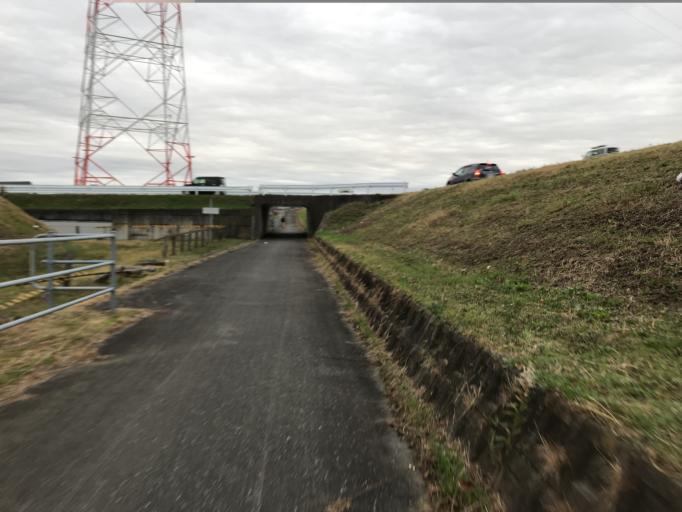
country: JP
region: Gifu
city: Ogaki
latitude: 35.3232
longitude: 136.6687
